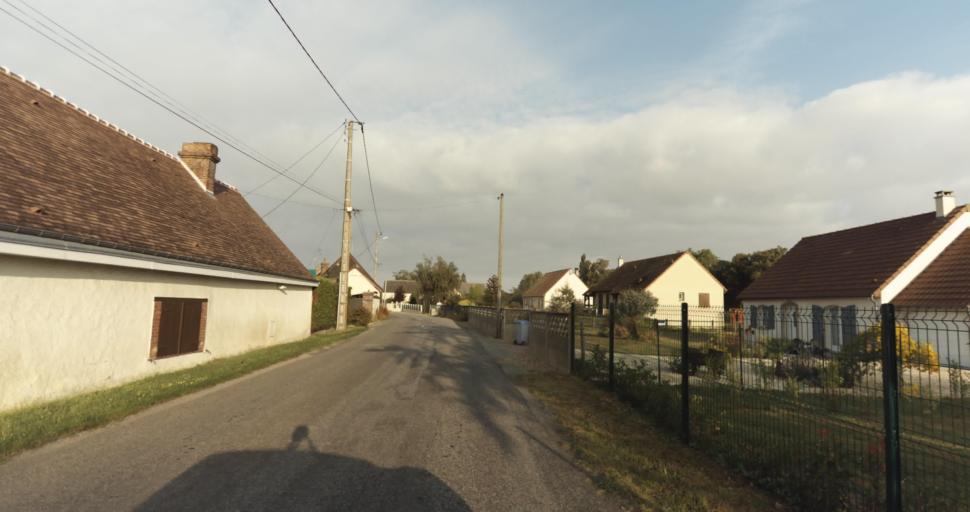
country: FR
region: Centre
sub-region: Departement d'Eure-et-Loir
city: Vert-en-Drouais
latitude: 48.7710
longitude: 1.3066
